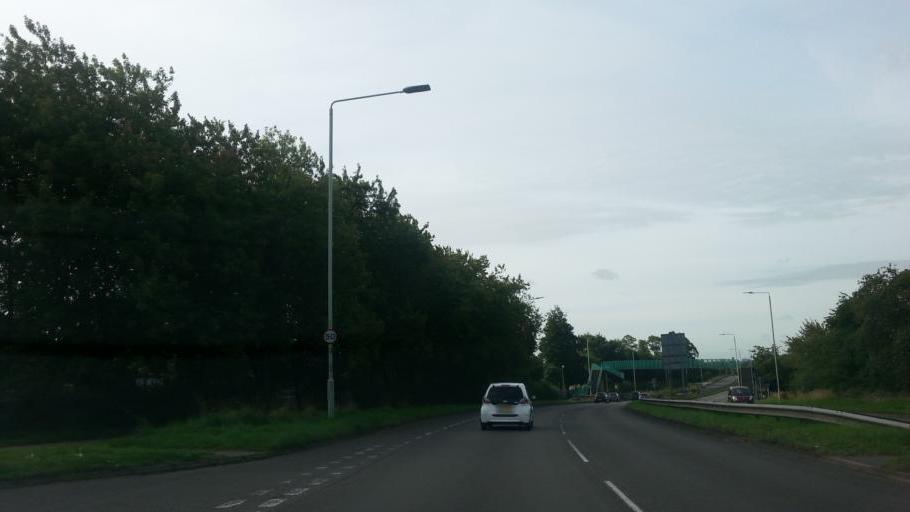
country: GB
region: England
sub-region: Leicestershire
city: Syston
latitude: 52.6817
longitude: -1.0926
